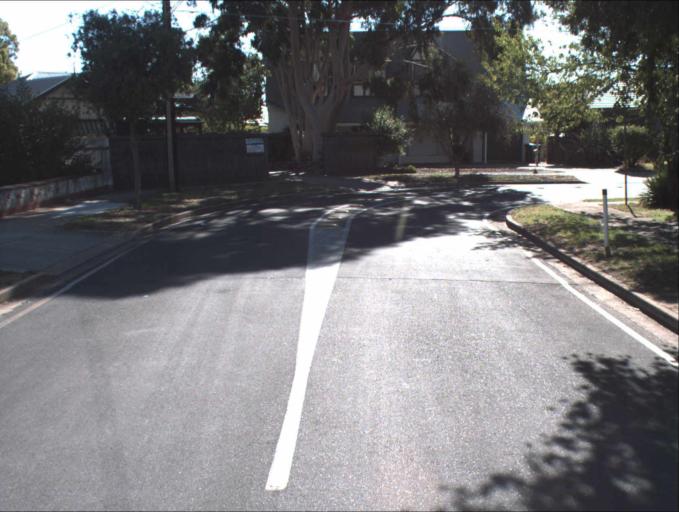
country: AU
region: South Australia
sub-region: Prospect
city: Prospect
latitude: -34.8768
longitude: 138.6074
